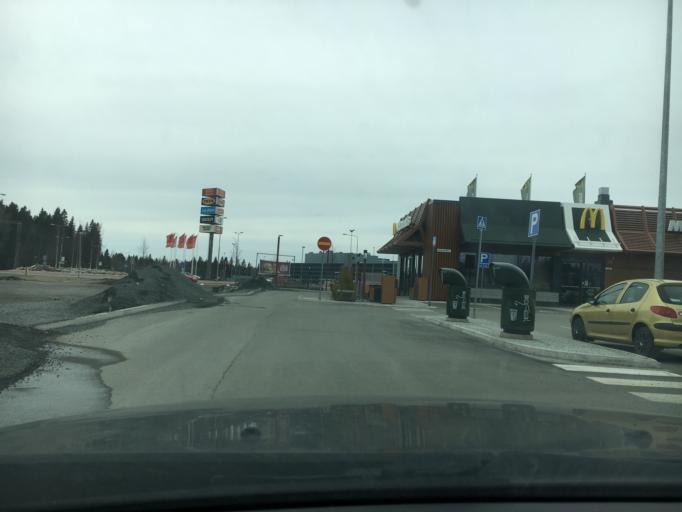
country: FI
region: Northern Savo
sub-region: Kuopio
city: Kuopio
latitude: 62.8204
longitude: 27.6066
